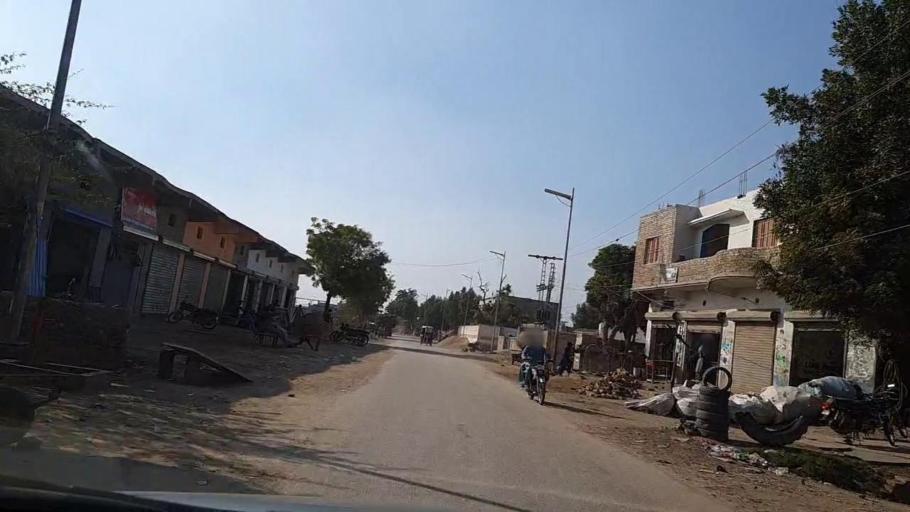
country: PK
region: Sindh
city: Sakrand
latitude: 26.1376
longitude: 68.2653
